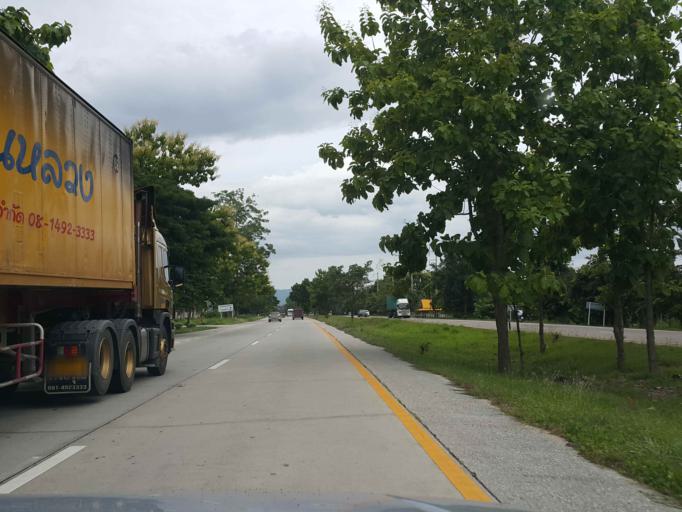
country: TH
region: Lampang
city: Lampang
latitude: 18.2958
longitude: 99.4162
